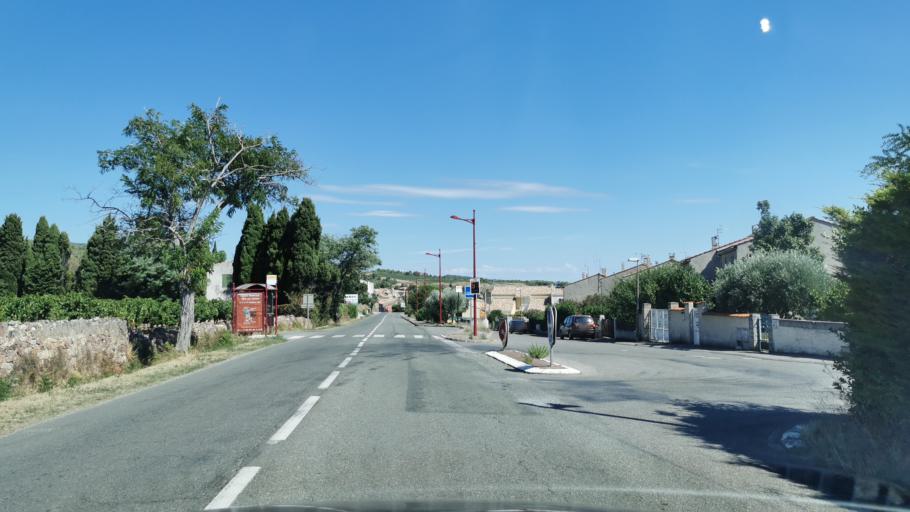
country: FR
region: Languedoc-Roussillon
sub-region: Departement de l'Aude
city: Caunes-Minervois
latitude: 43.3243
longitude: 2.5185
